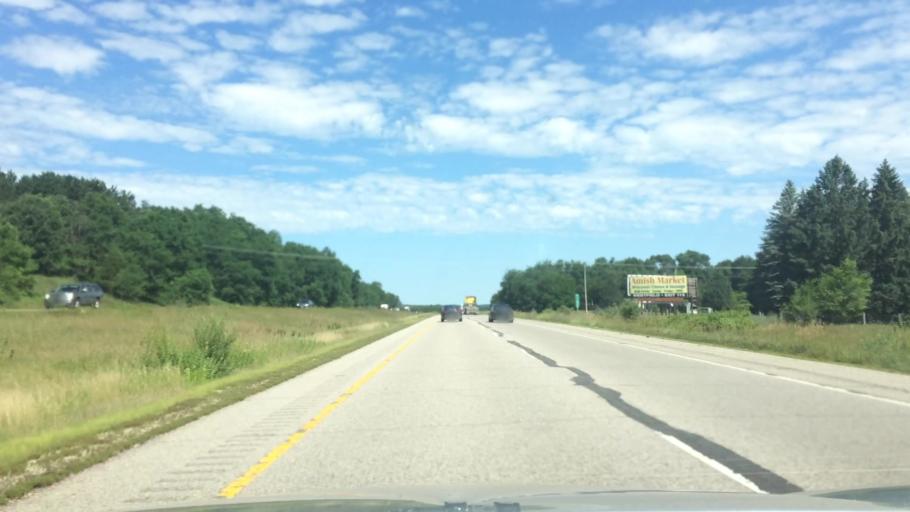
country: US
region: Wisconsin
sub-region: Marquette County
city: Westfield
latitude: 43.7239
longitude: -89.4803
